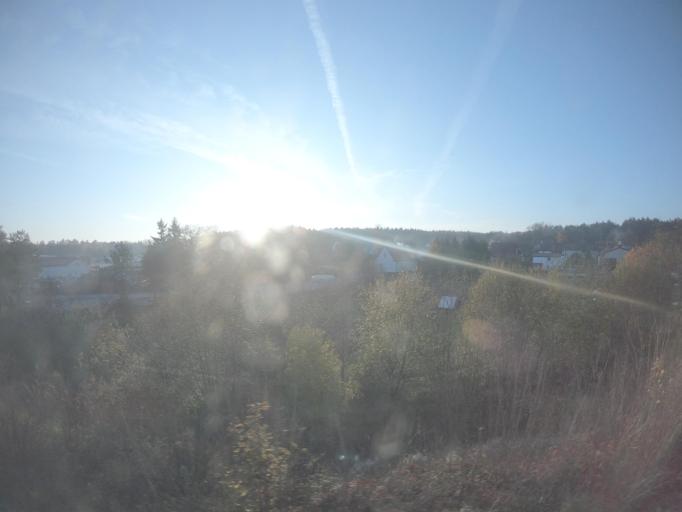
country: PL
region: Lubusz
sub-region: Powiat slubicki
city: Rzepin
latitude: 52.3397
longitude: 14.8301
